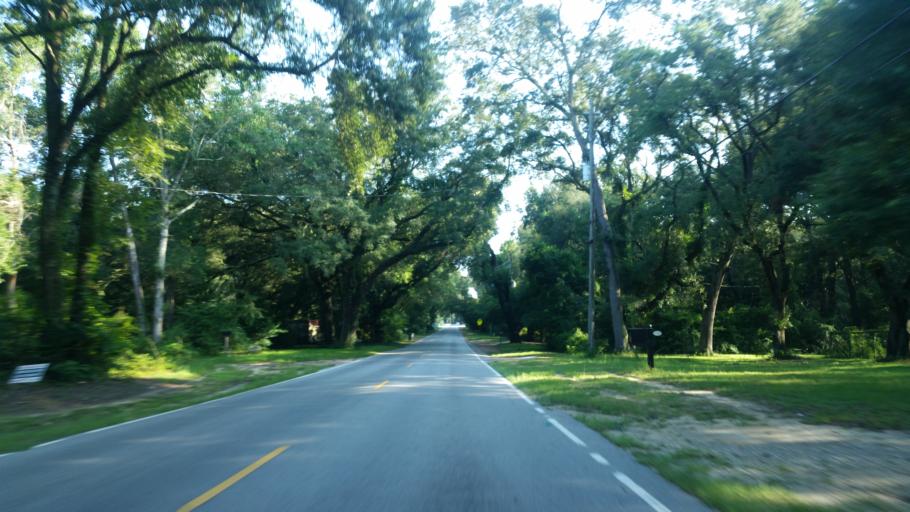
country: US
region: Florida
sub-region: Escambia County
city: Bellview
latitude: 30.4461
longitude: -87.3161
